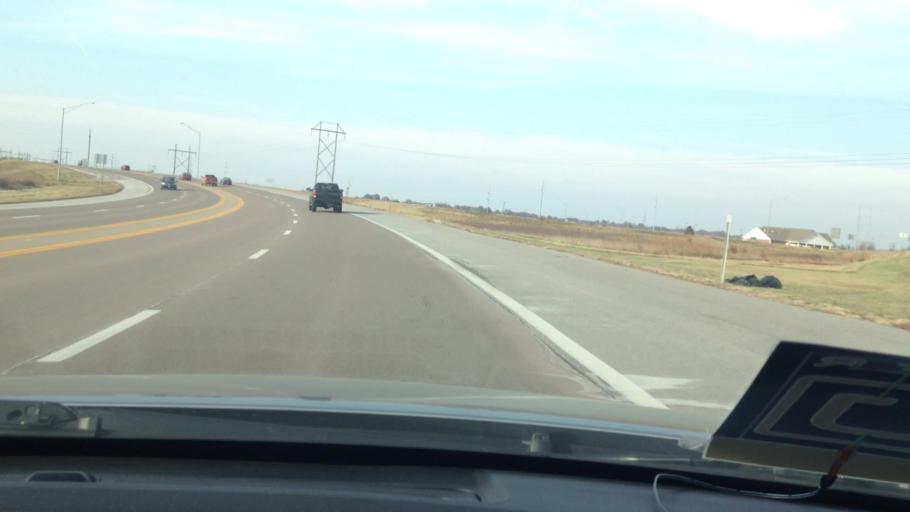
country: US
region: Missouri
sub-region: Henry County
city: Clinton
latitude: 38.3834
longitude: -93.7521
